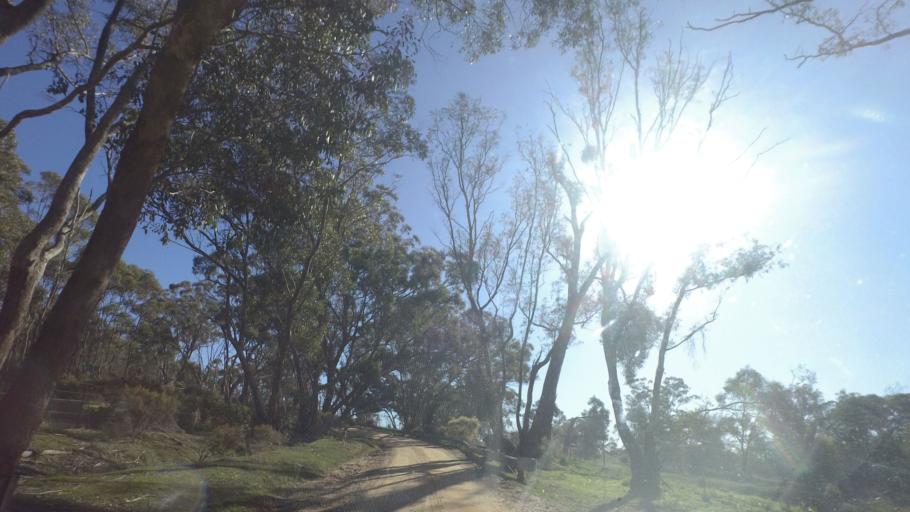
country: AU
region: Victoria
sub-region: Mount Alexander
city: Castlemaine
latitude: -37.0335
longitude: 144.2755
